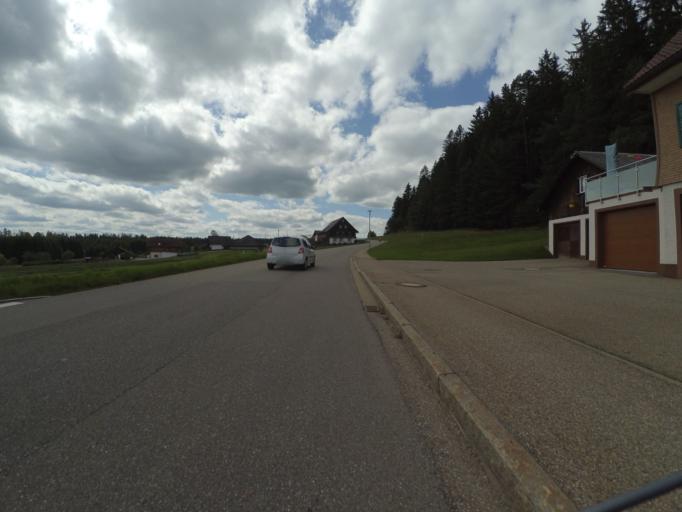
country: DE
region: Baden-Wuerttemberg
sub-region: Freiburg Region
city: Eisenbach
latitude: 47.9470
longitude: 8.2759
